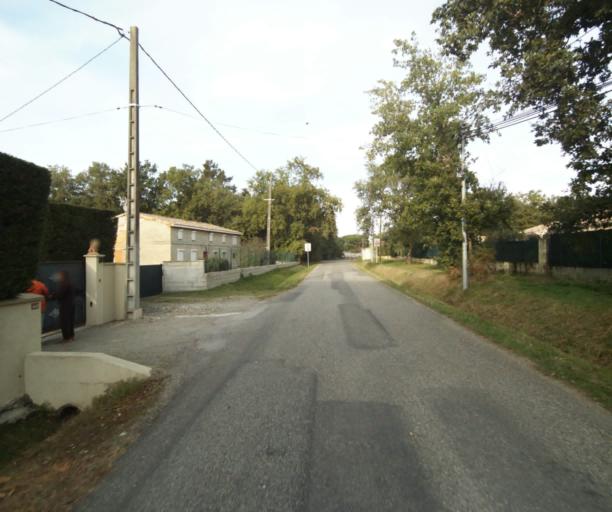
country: FR
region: Midi-Pyrenees
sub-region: Departement du Tarn-et-Garonne
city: Campsas
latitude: 43.8941
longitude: 1.3221
